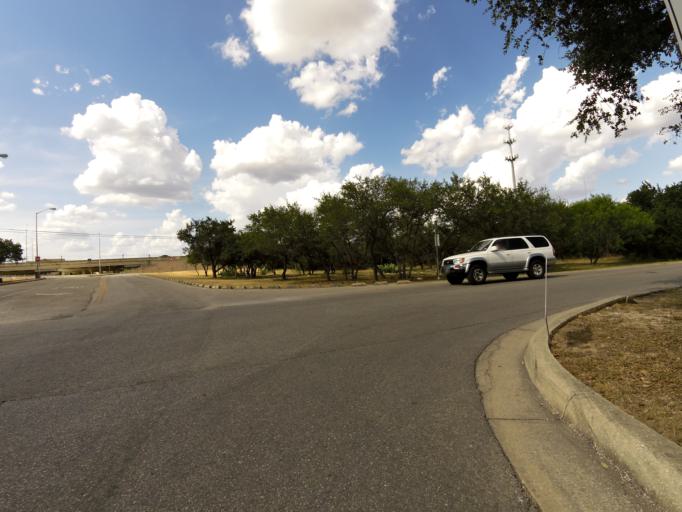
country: US
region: Texas
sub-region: Bexar County
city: Helotes
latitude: 29.5862
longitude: -98.6277
